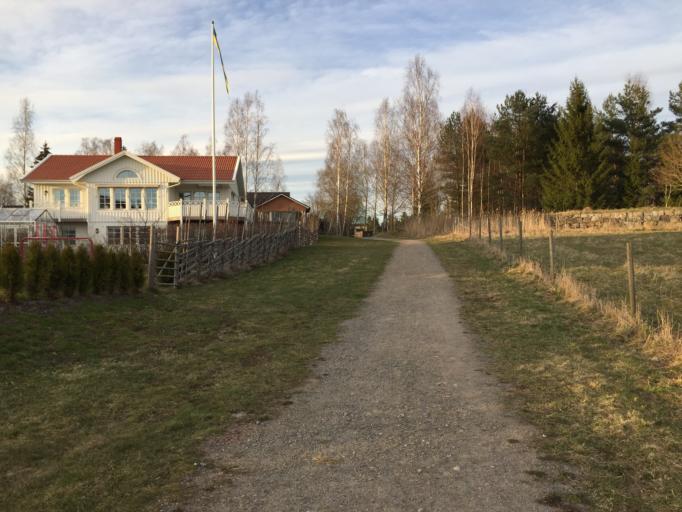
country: SE
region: Soedermanland
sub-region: Katrineholms Kommun
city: Katrineholm
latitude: 58.9779
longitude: 16.1961
